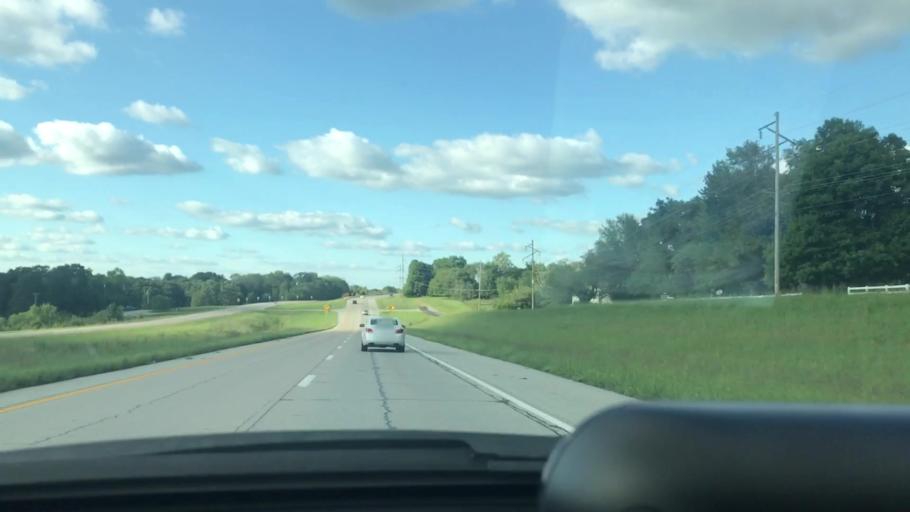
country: US
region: Missouri
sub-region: Pettis County
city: Sedalia
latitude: 38.6311
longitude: -93.2672
